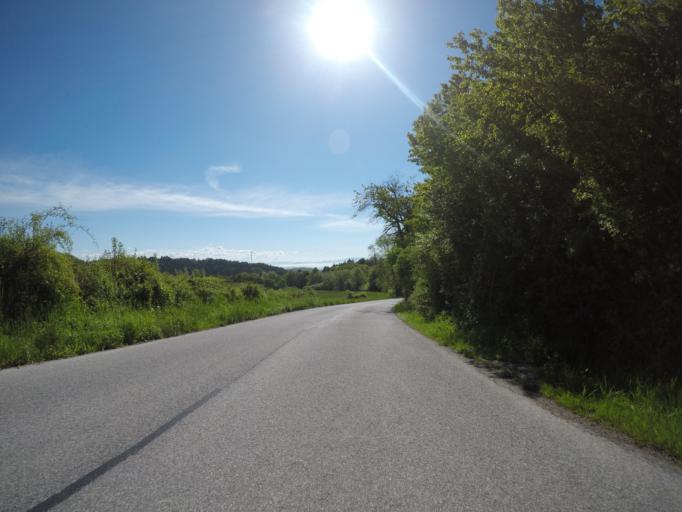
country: SK
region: Banskobystricky
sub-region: Okres Banska Bystrica
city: Zvolen
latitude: 48.6090
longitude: 19.0264
